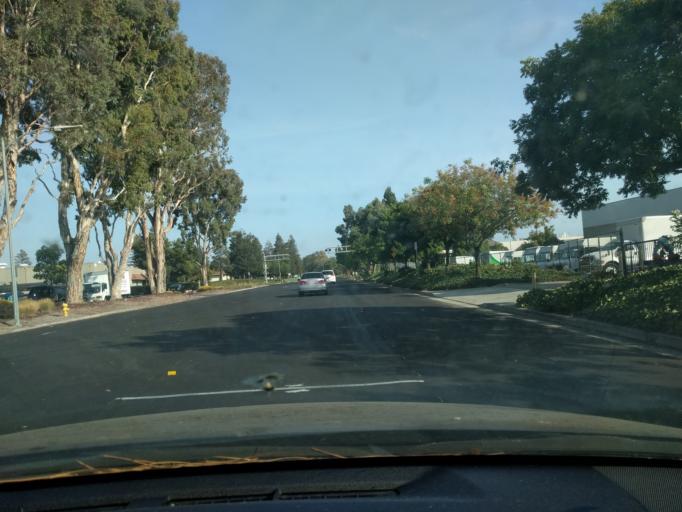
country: US
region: California
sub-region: Santa Clara County
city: Milpitas
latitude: 37.3881
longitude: -121.9179
